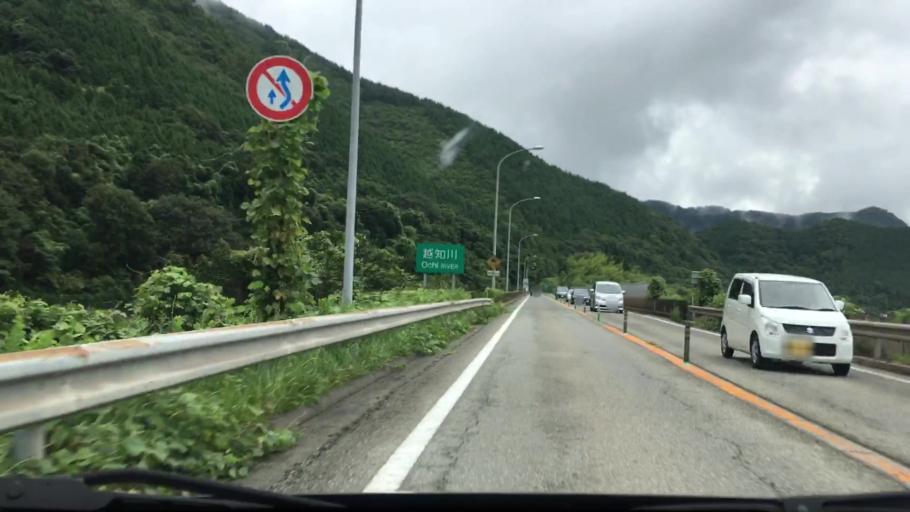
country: JP
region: Hyogo
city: Nishiwaki
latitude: 35.0435
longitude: 134.7676
